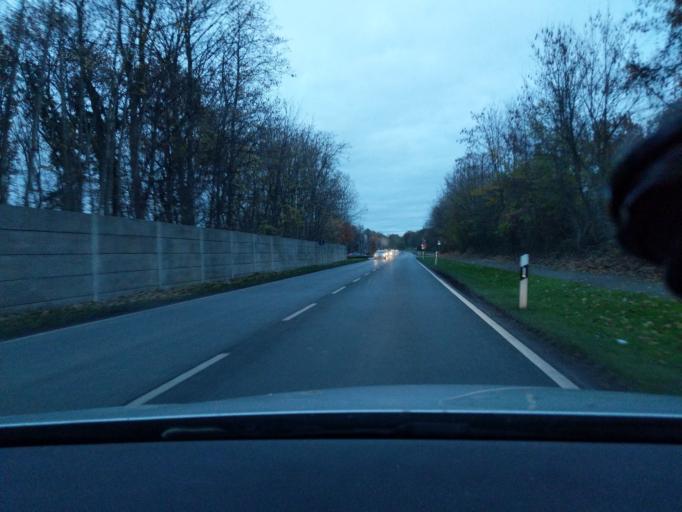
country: DE
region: North Rhine-Westphalia
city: Waltrop
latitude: 51.6170
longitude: 7.4615
